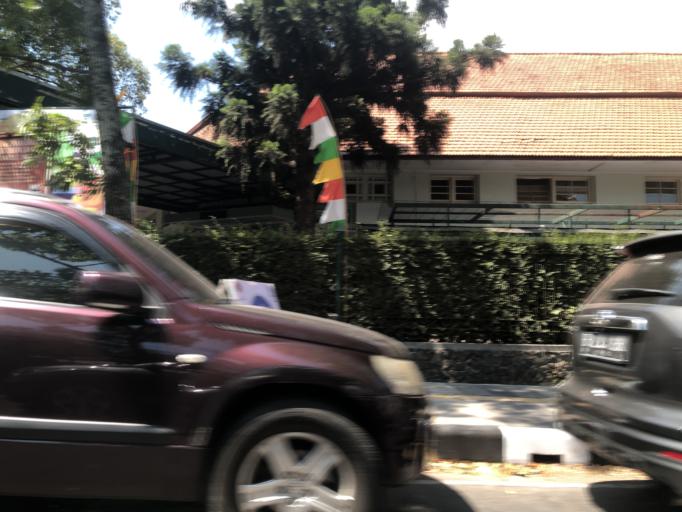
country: ID
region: West Java
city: Bandung
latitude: -6.9112
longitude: 107.6309
